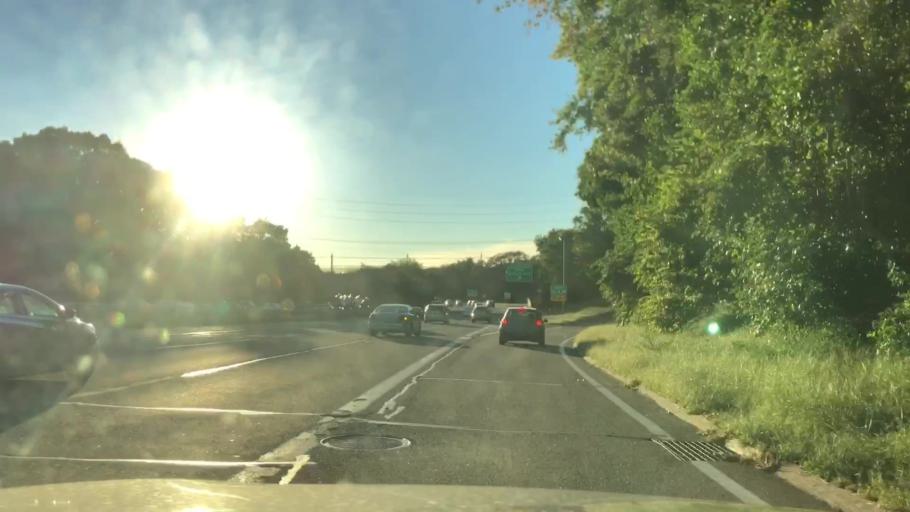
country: US
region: New York
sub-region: Nassau County
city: Malverne
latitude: 40.6834
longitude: -73.6840
